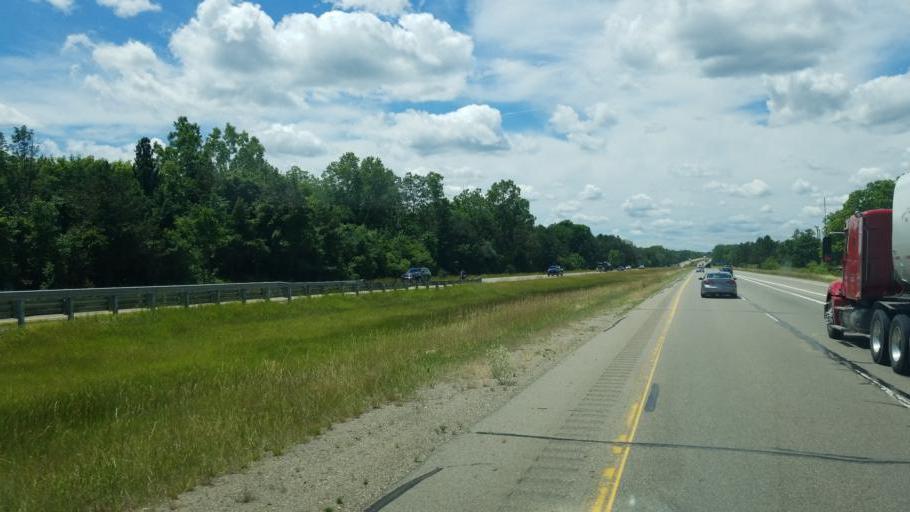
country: US
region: Michigan
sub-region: Ingham County
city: Holt
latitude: 42.6729
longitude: -84.5005
